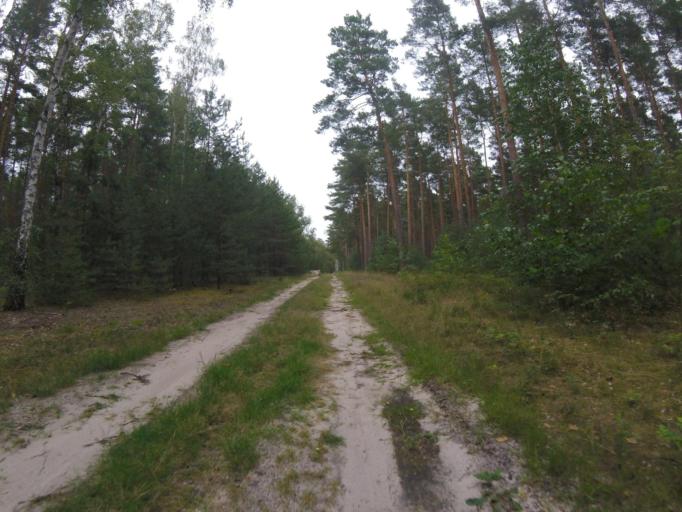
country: DE
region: Brandenburg
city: Gross Koris
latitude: 52.2038
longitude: 13.6876
